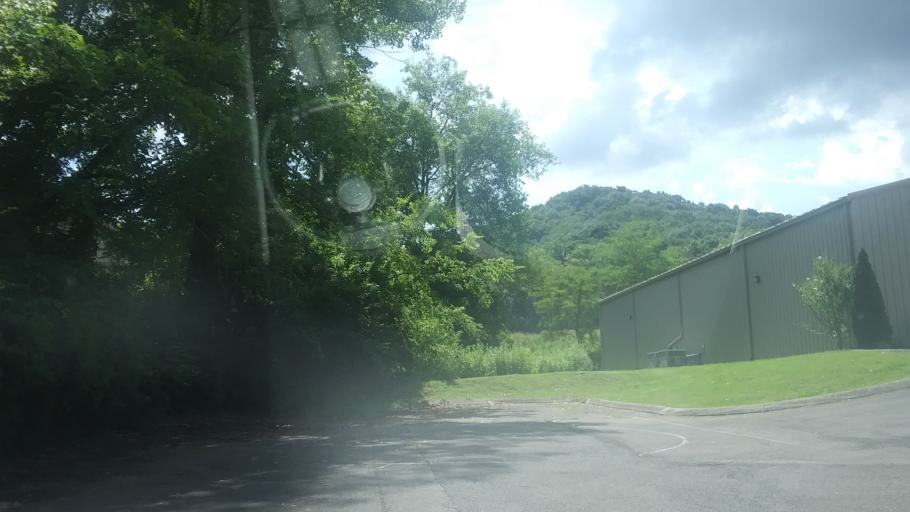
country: US
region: Tennessee
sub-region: Davidson County
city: Belle Meade
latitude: 36.1118
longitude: -86.9198
